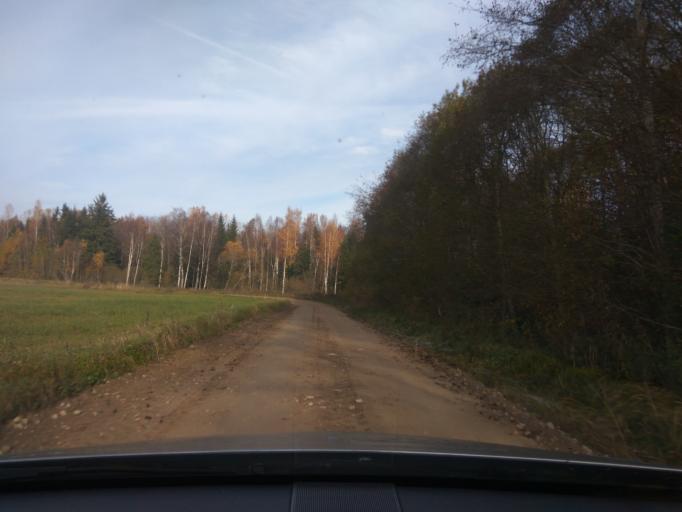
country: LV
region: Aizpute
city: Aizpute
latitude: 56.8421
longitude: 21.7136
